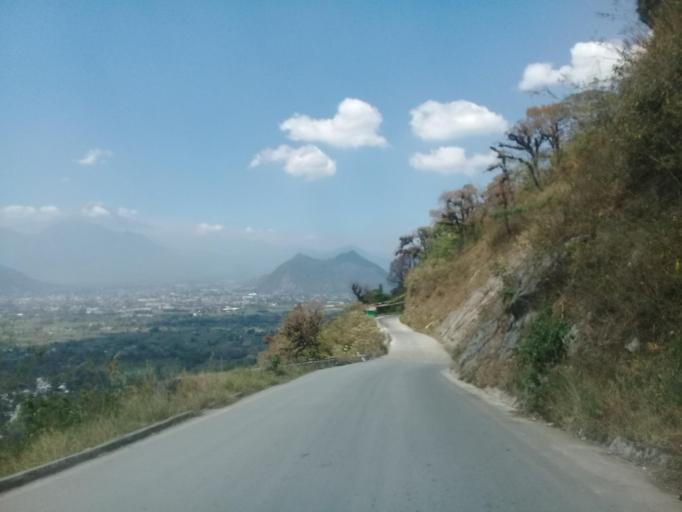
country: MX
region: Veracruz
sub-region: Tlilapan
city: Tonalixco
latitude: 18.8069
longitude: -97.0603
